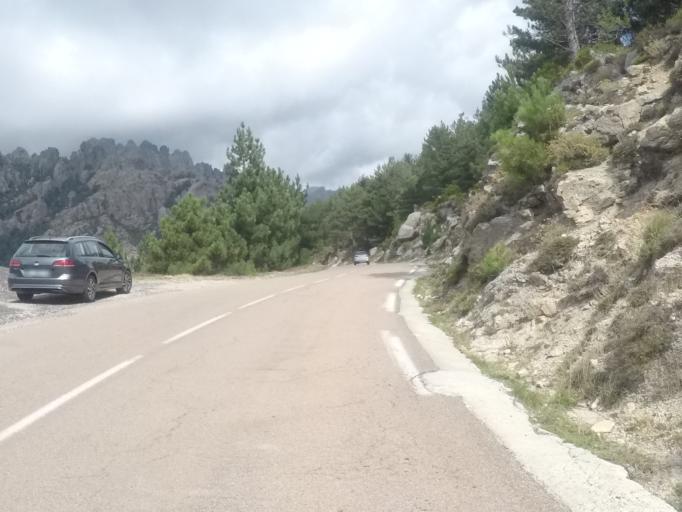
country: FR
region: Corsica
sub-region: Departement de la Corse-du-Sud
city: Zonza
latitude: 41.7898
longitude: 9.2218
